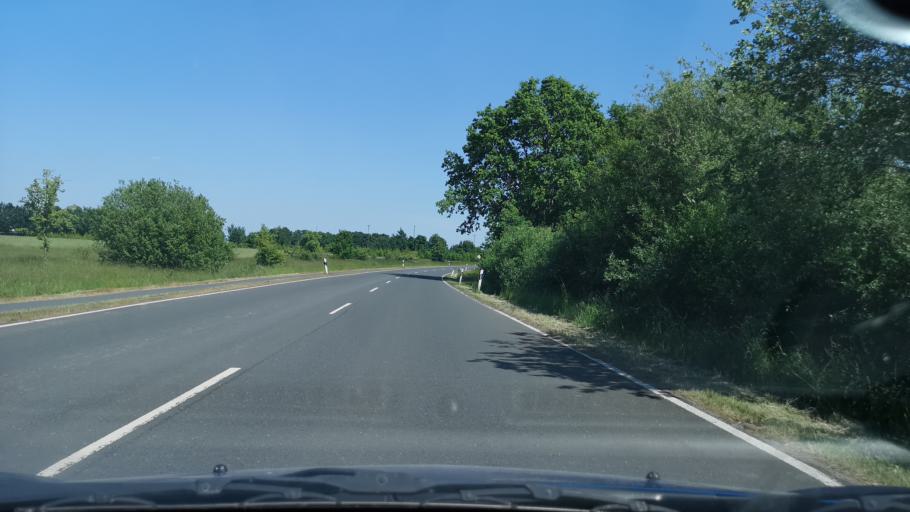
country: DE
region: Lower Saxony
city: Garbsen-Mitte
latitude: 52.4500
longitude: 9.5748
